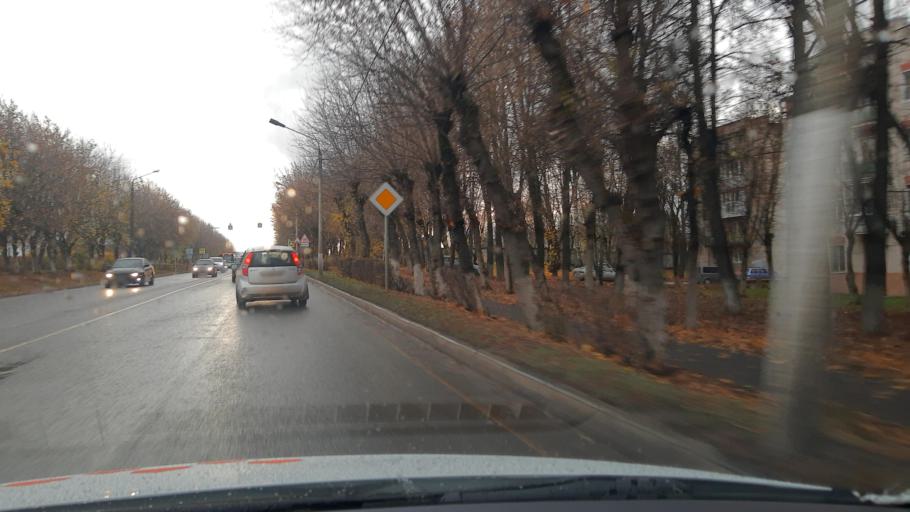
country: RU
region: Moskovskaya
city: Noginsk
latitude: 55.8393
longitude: 38.3954
